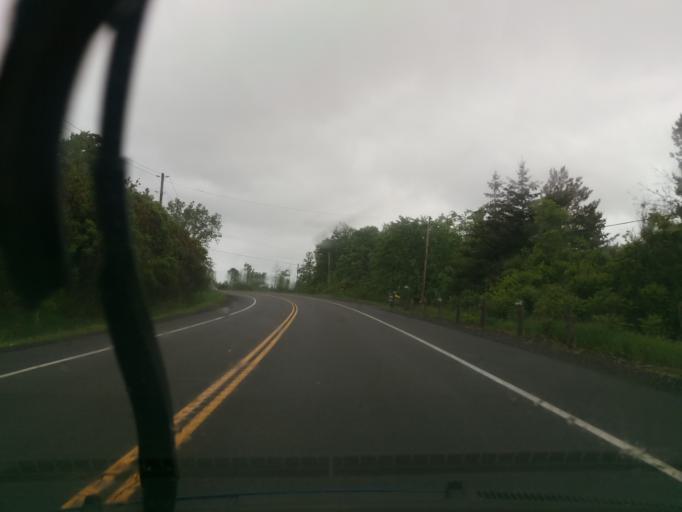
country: CA
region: Ontario
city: Clarence-Rockland
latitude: 45.5147
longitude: -75.4565
